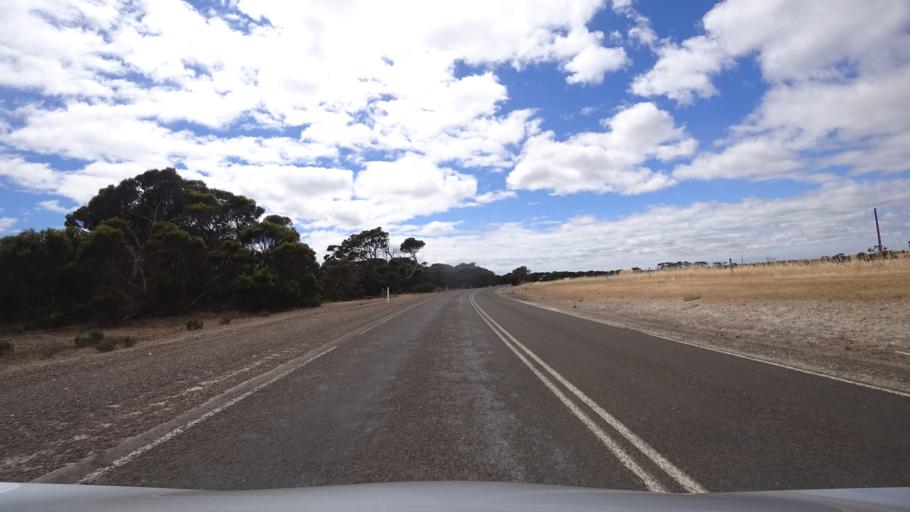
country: AU
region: South Australia
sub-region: Kangaroo Island
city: Kingscote
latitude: -35.6262
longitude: 137.5527
